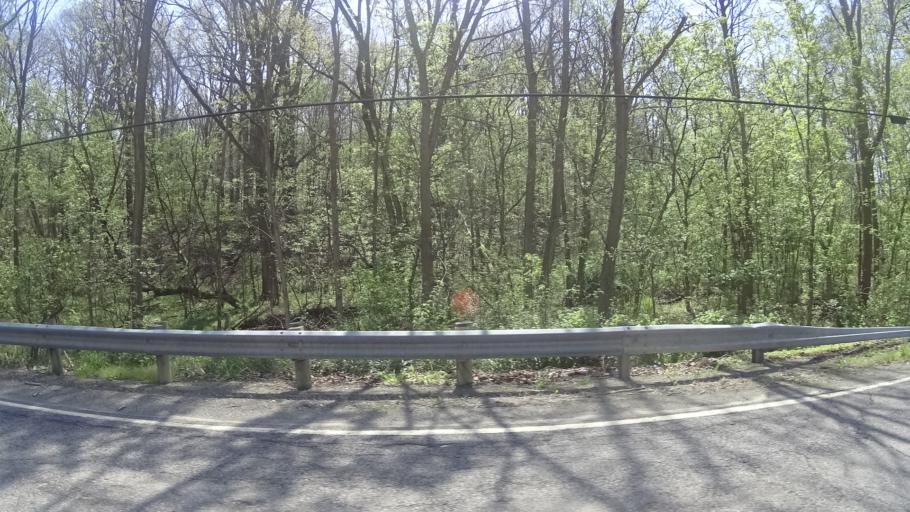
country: US
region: Ohio
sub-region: Lorain County
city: Lagrange
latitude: 41.2797
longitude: -82.1505
